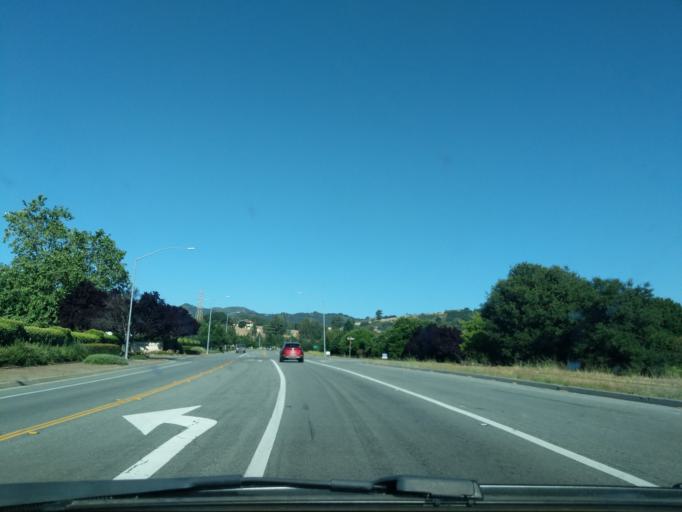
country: US
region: California
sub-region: Santa Clara County
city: San Martin
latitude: 37.0927
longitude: -121.6417
